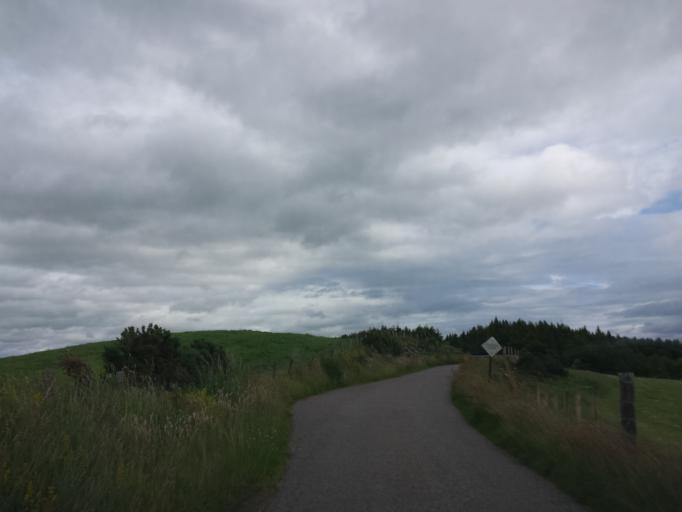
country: GB
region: Scotland
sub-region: Highland
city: Fortrose
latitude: 57.5116
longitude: -4.0313
